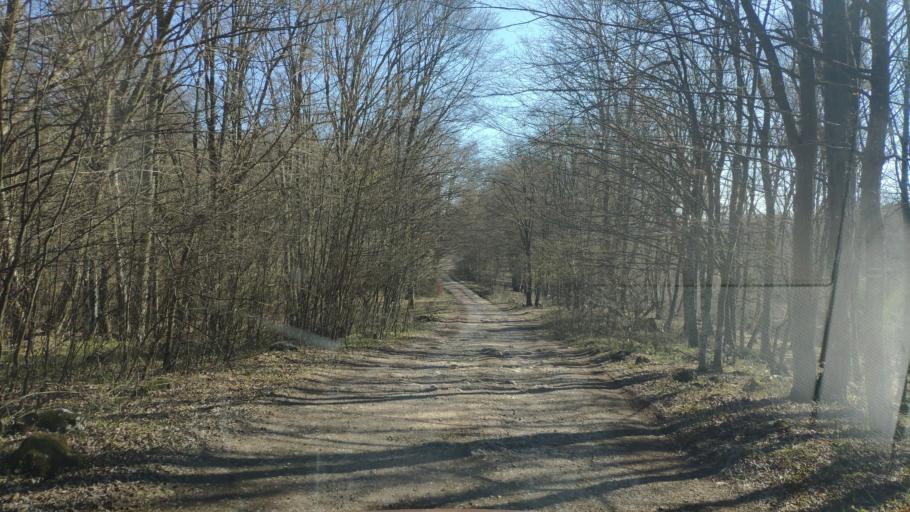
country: SK
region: Kosicky
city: Roznava
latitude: 48.5998
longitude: 20.4107
